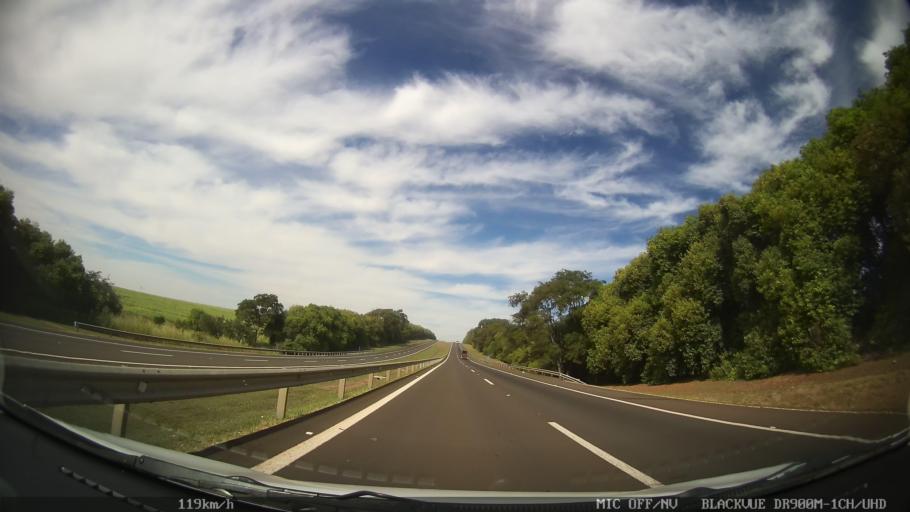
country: BR
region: Sao Paulo
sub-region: Matao
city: Matao
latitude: -21.6222
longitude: -48.4123
